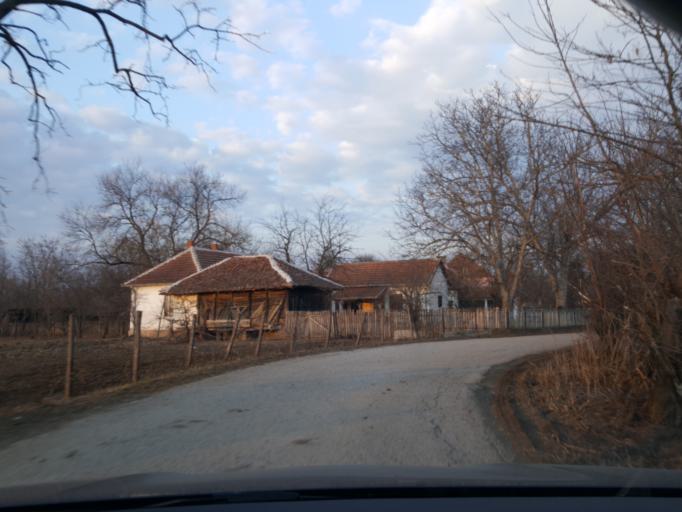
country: RS
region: Central Serbia
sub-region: Nisavski Okrug
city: Aleksinac
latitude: 43.5716
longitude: 21.6416
